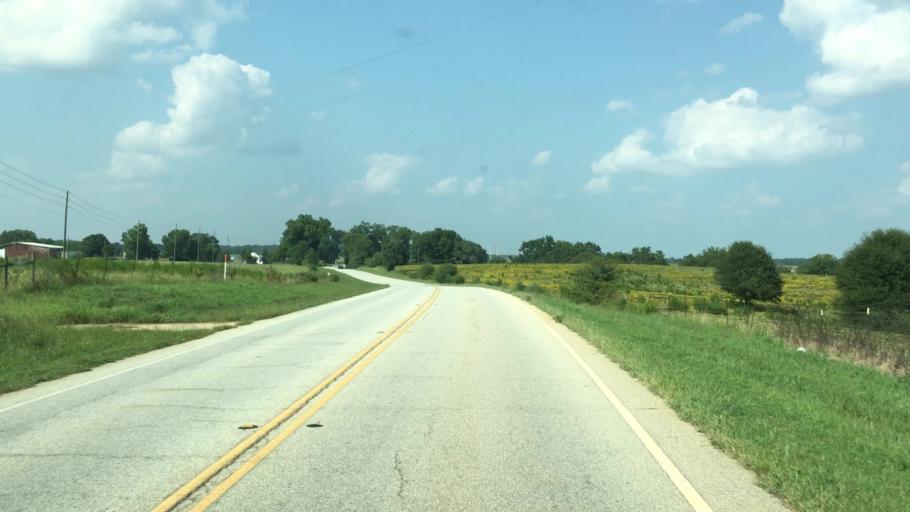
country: US
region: Georgia
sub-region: Newton County
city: Covington
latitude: 33.4827
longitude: -83.7440
